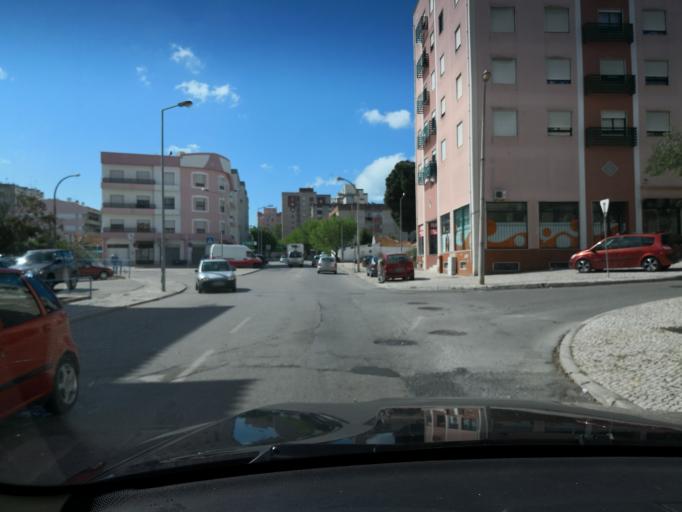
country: PT
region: Setubal
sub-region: Setubal
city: Setubal
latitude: 38.5281
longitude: -8.8704
